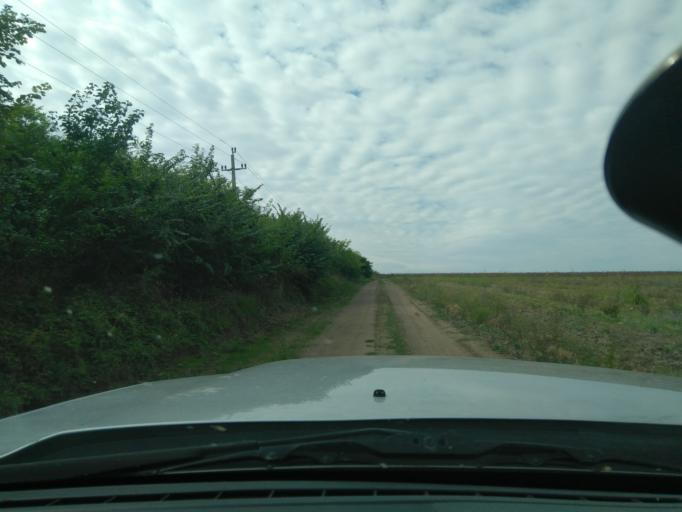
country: HU
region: Fejer
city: Val
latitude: 47.3670
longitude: 18.7041
